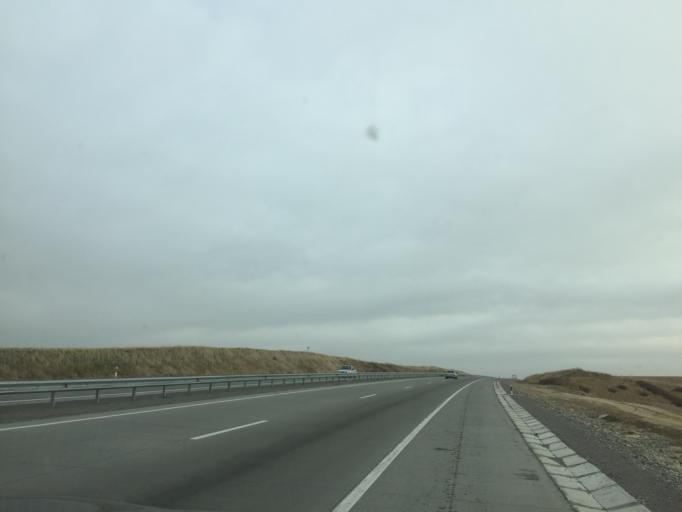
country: KZ
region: Ongtustik Qazaqstan
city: Aksu
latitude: 42.4449
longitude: 69.7312
